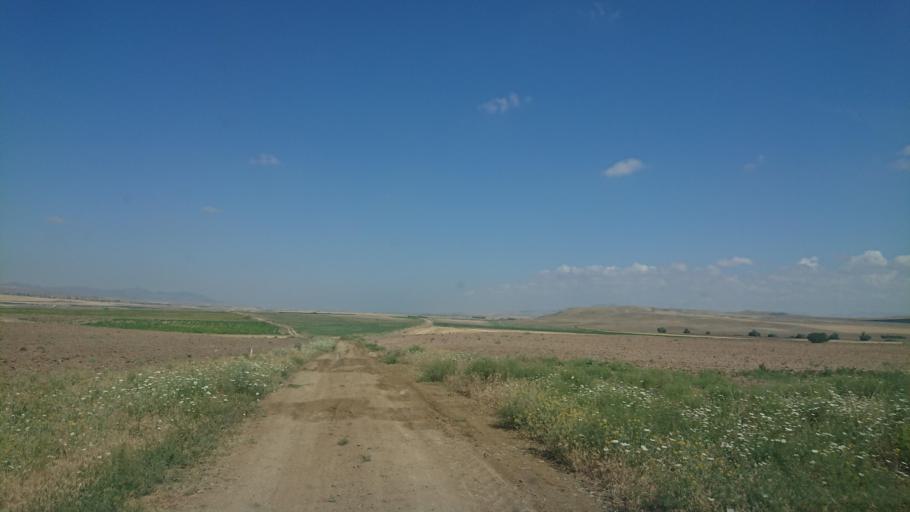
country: TR
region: Aksaray
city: Agacoren
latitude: 38.9626
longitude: 33.9280
